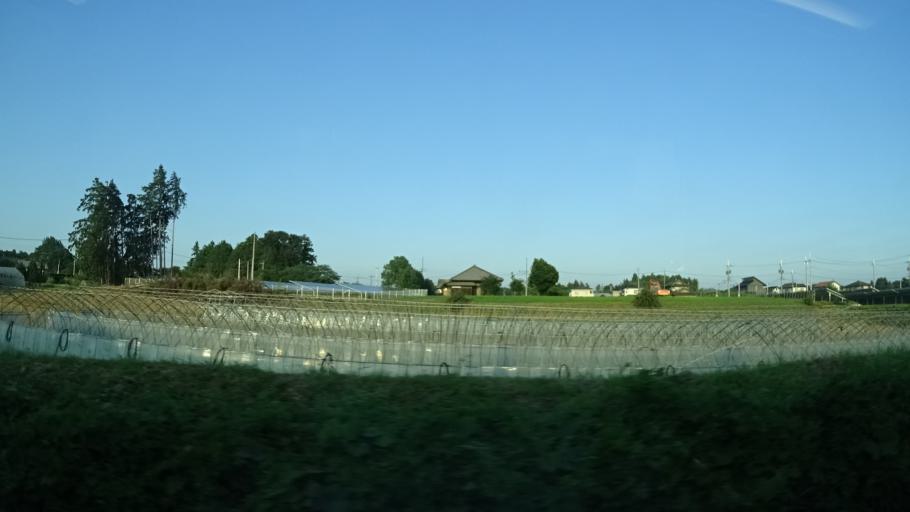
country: JP
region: Ibaraki
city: Ishioka
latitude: 36.2352
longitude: 140.2898
